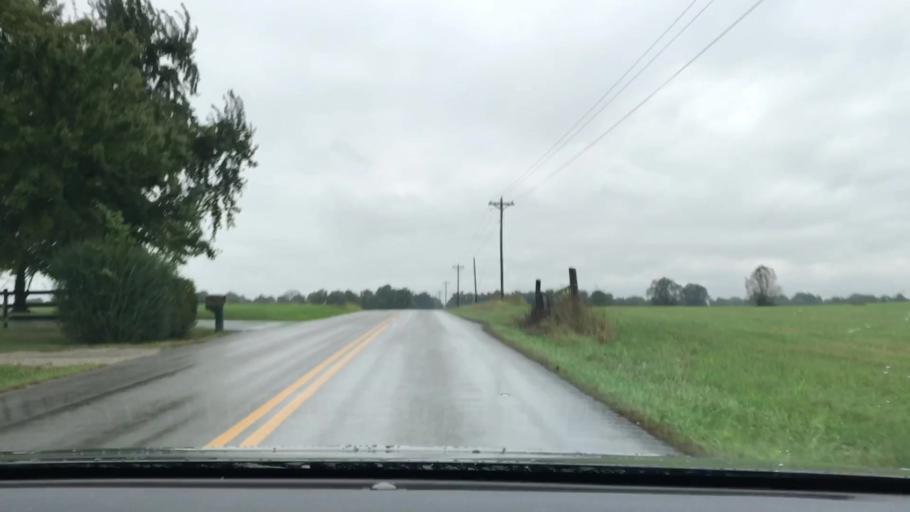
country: US
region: Kentucky
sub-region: McLean County
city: Calhoun
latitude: 37.4042
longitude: -87.2642
